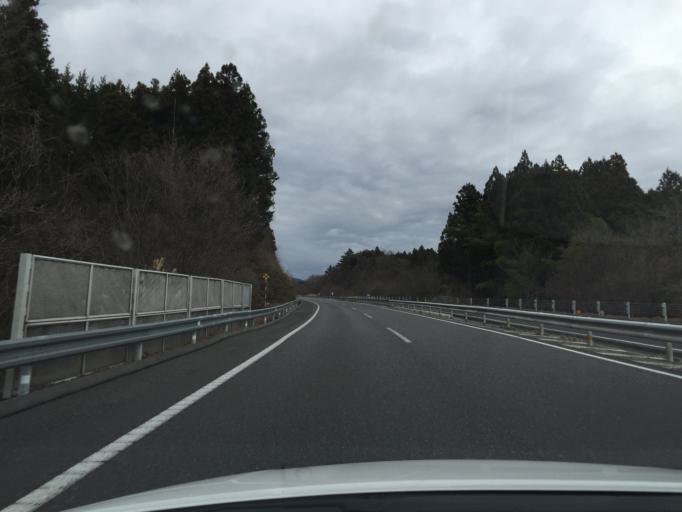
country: JP
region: Fukushima
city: Funehikimachi-funehiki
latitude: 37.3018
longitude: 140.6145
